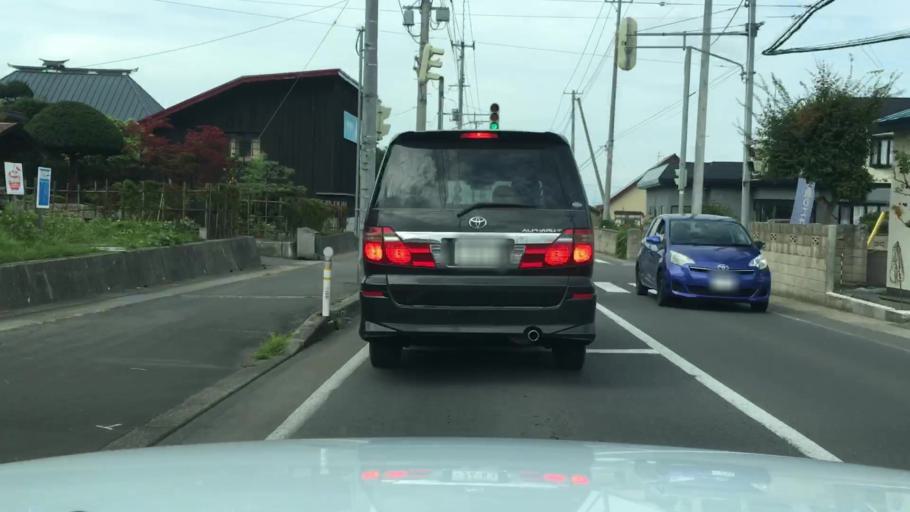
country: JP
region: Aomori
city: Hirosaki
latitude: 40.5897
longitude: 140.4555
